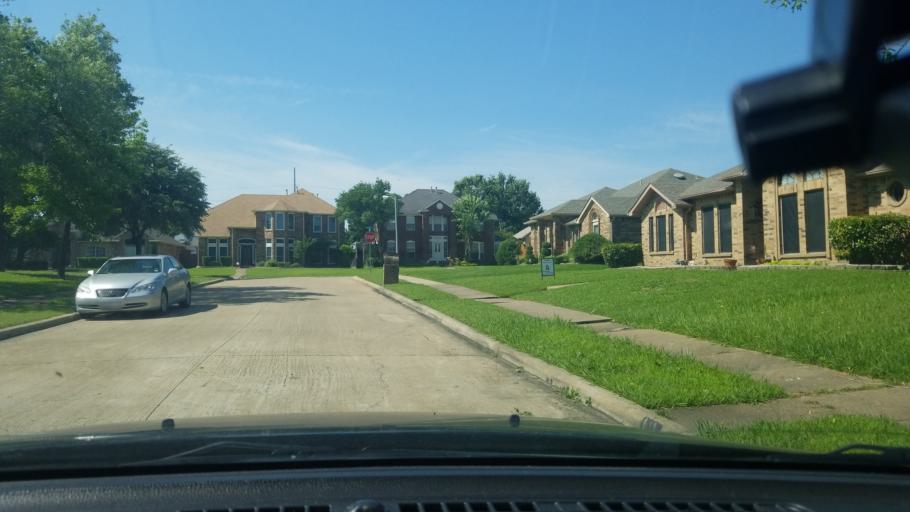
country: US
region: Texas
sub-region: Dallas County
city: Mesquite
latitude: 32.7774
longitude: -96.5887
